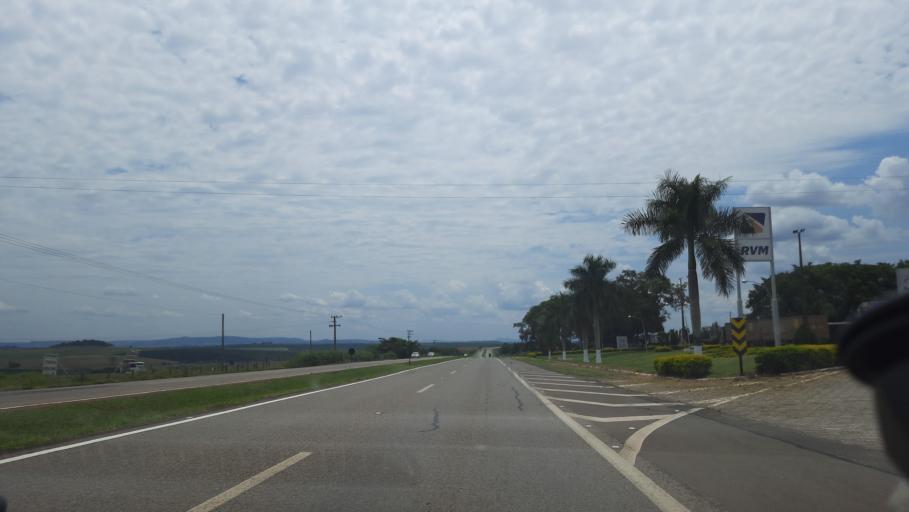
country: BR
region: Sao Paulo
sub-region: Casa Branca
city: Casa Branca
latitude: -21.7206
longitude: -47.0801
